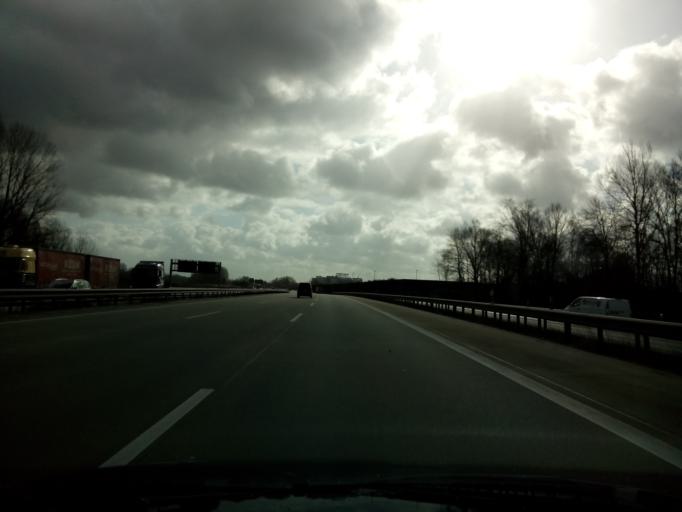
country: DE
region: Lower Saxony
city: Ritterhude
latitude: 53.1421
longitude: 8.7391
